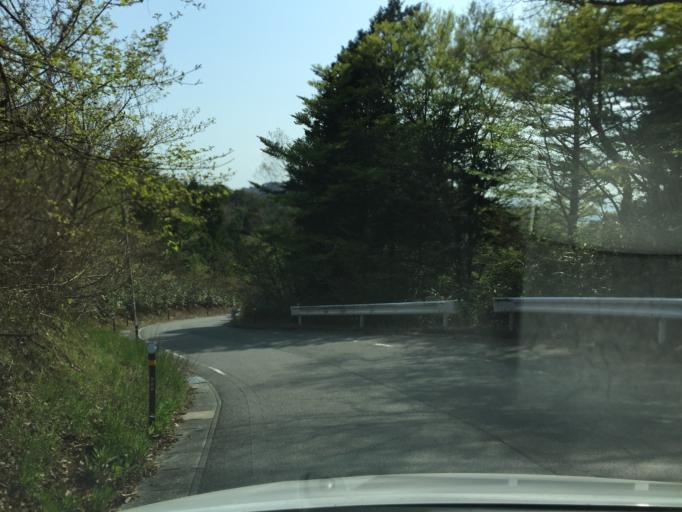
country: JP
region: Fukushima
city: Iwaki
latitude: 37.1922
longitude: 140.8521
